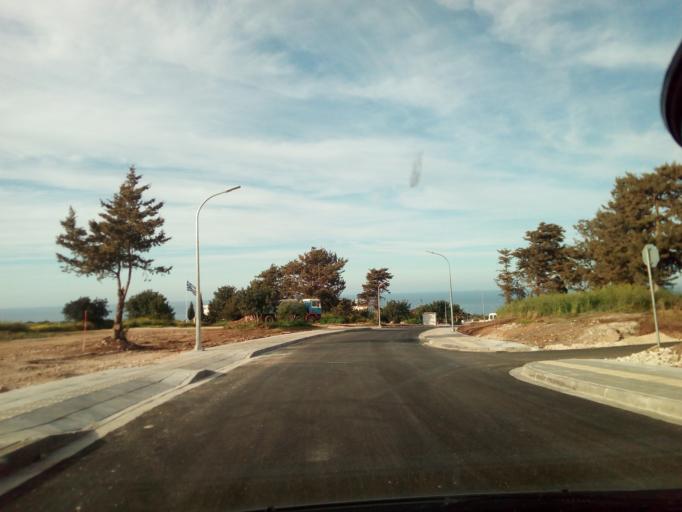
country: CY
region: Pafos
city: Polis
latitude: 35.0278
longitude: 32.3612
